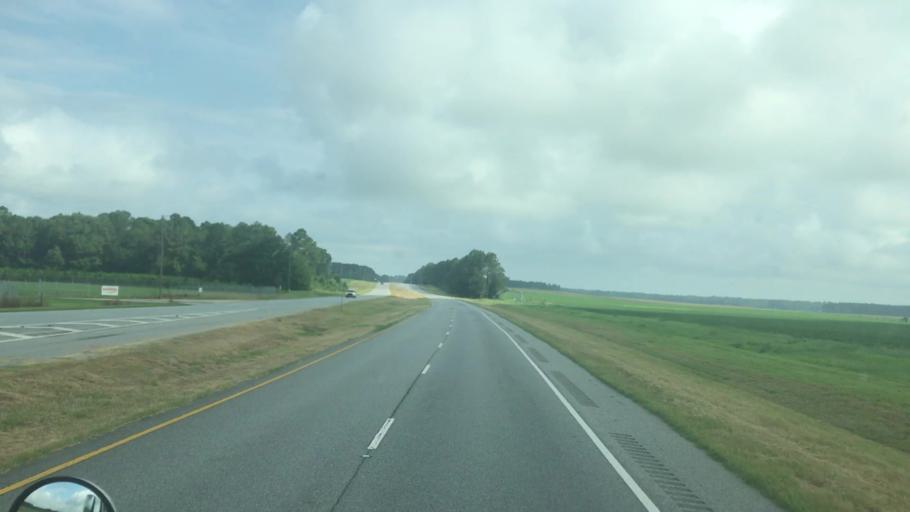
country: US
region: Georgia
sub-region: Miller County
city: Colquitt
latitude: 31.1859
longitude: -84.7628
